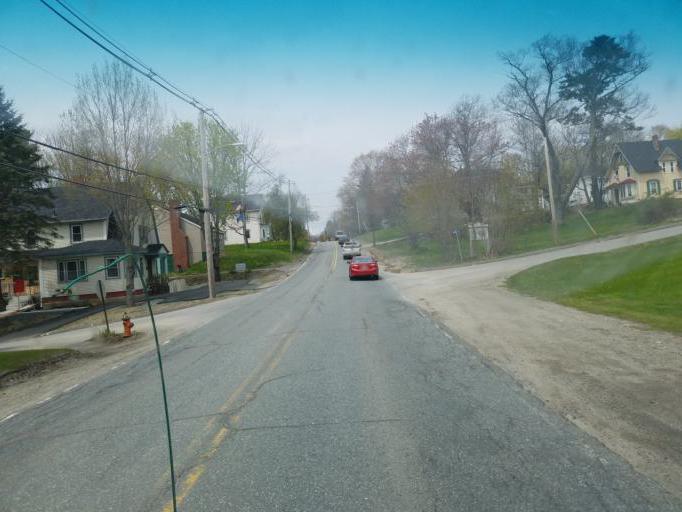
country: US
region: Maine
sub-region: Hancock County
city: Ellsworth
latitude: 44.5454
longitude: -68.4219
